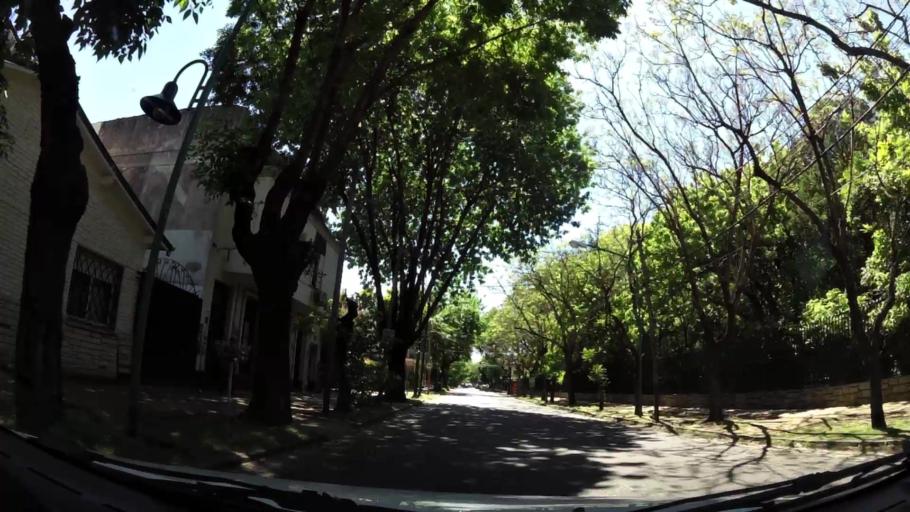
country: AR
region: Buenos Aires
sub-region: Partido de Vicente Lopez
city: Olivos
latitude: -34.5206
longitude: -58.5048
